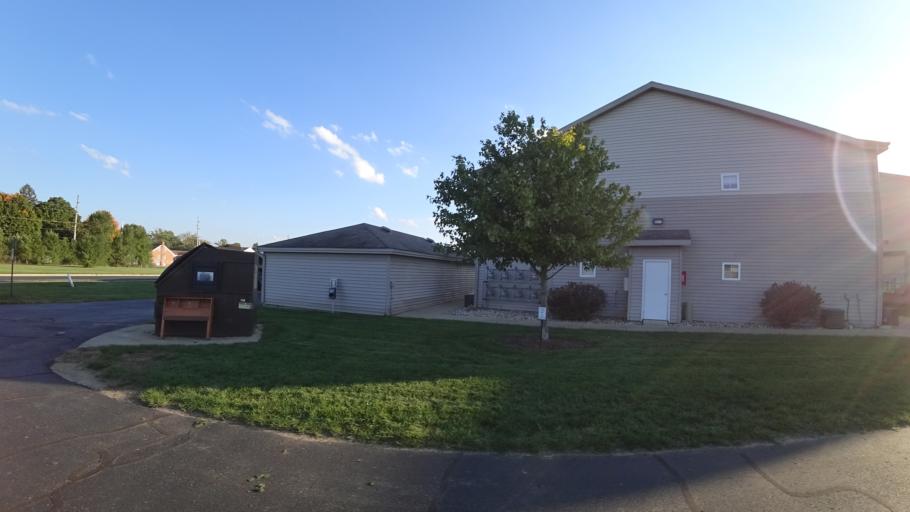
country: US
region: Michigan
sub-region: Saint Joseph County
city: Three Rivers
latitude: 41.9459
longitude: -85.6467
